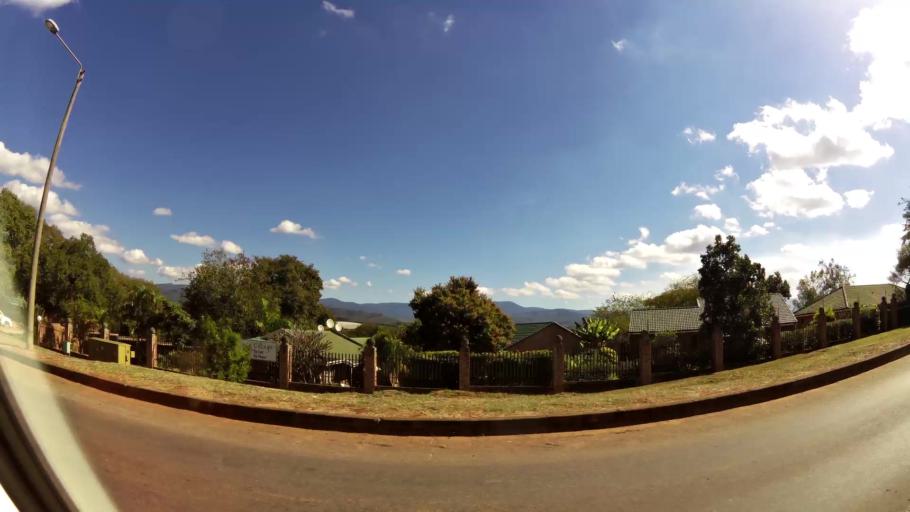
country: ZA
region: Limpopo
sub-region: Mopani District Municipality
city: Tzaneen
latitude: -23.8202
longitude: 30.1440
